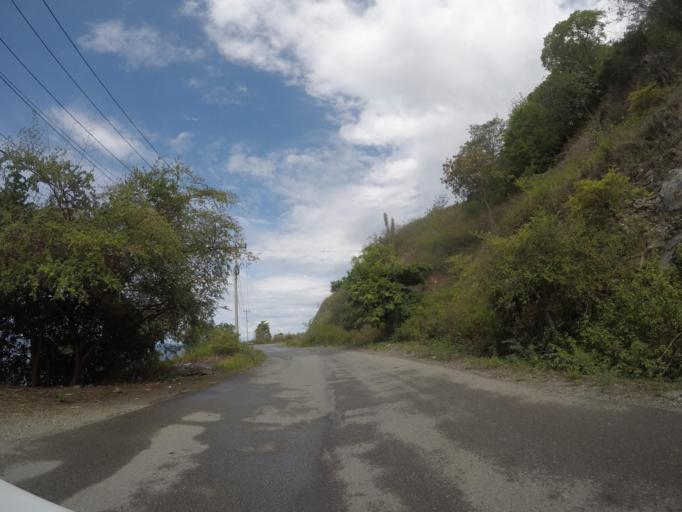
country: TL
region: Liquica
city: Maubara
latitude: -8.6347
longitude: 125.1442
